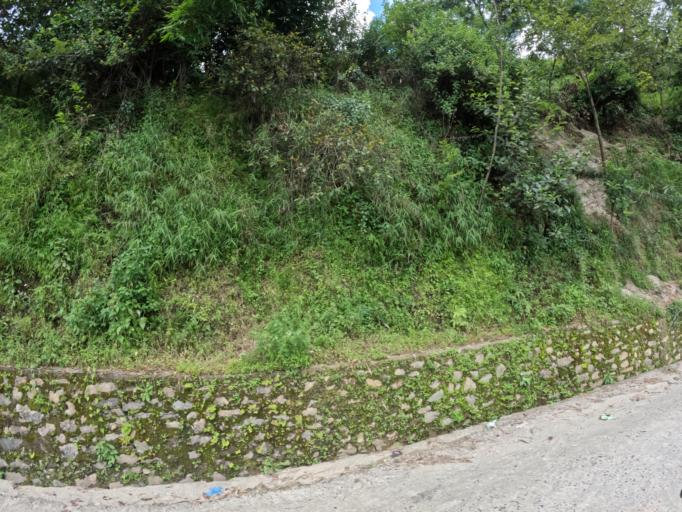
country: NP
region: Central Region
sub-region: Bagmati Zone
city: Kathmandu
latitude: 27.8009
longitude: 85.3288
